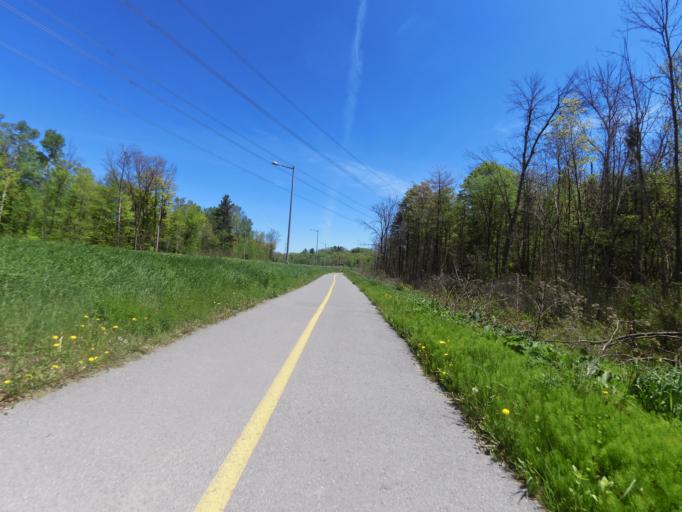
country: CA
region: Ontario
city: Ottawa
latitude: 45.4339
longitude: -75.7602
